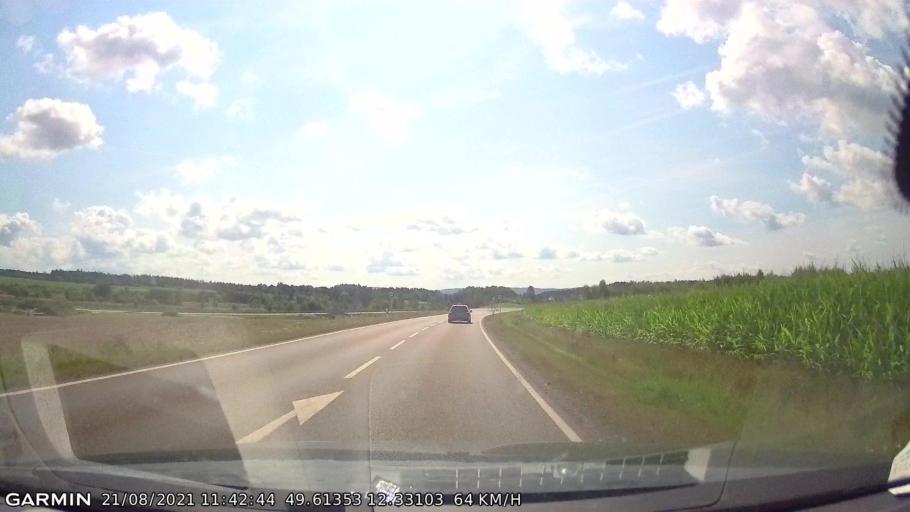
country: DE
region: Bavaria
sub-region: Upper Palatinate
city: Vohenstrauss
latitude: 49.6137
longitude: 12.3310
